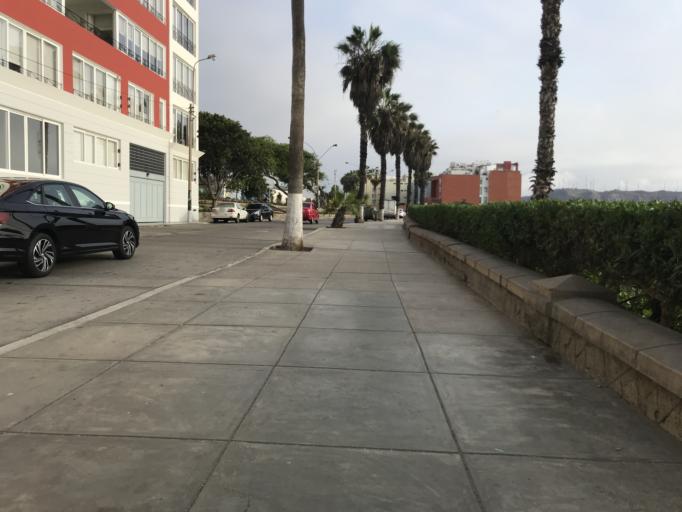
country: PE
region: Lima
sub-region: Lima
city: Surco
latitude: -12.1444
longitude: -77.0246
